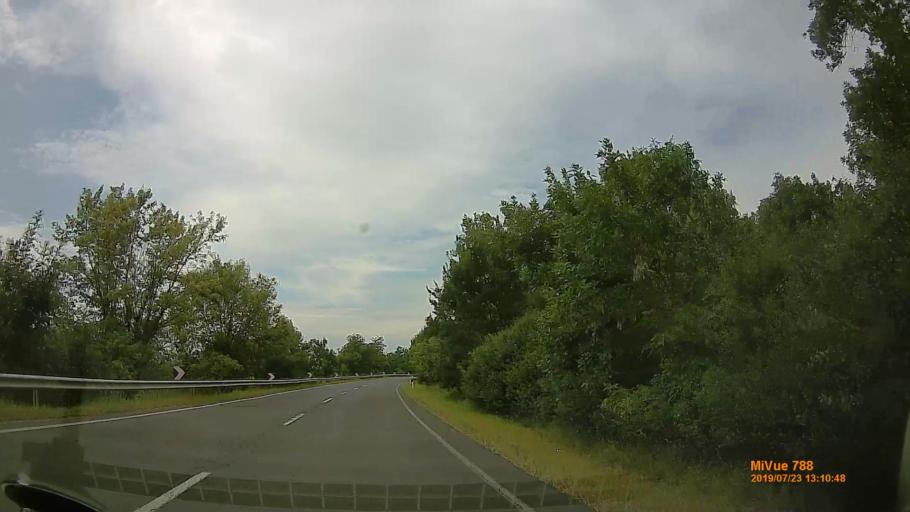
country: HU
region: Szabolcs-Szatmar-Bereg
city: Tiszavasvari
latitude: 47.9255
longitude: 21.2846
